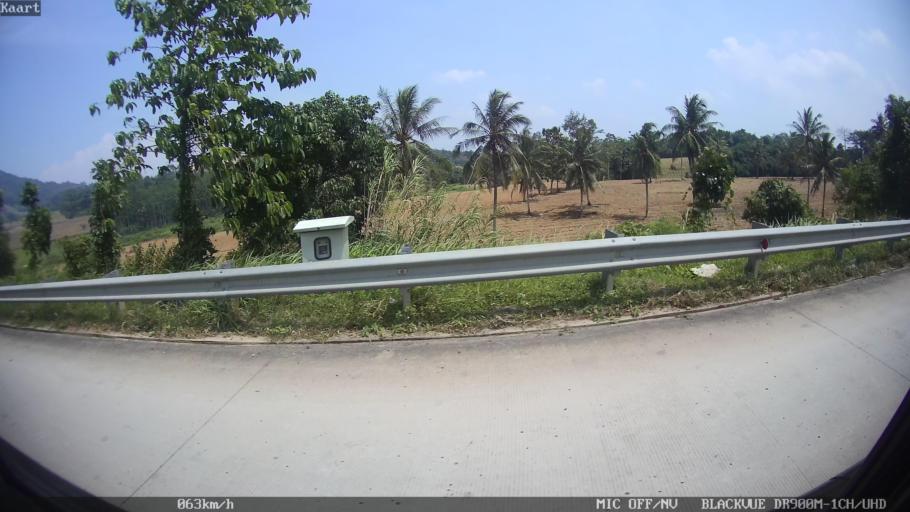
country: ID
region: Lampung
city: Panjang
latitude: -5.3980
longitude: 105.3476
